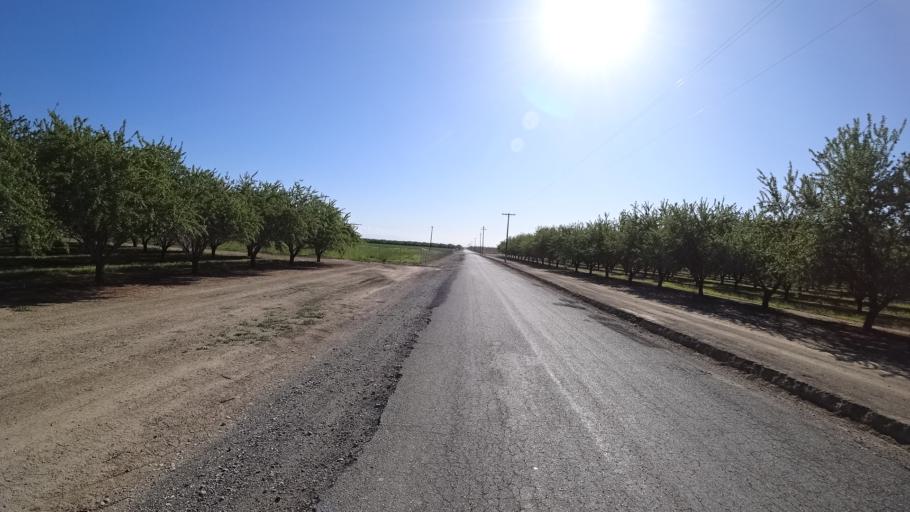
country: US
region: California
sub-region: Glenn County
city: Hamilton City
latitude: 39.6782
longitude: -122.0658
